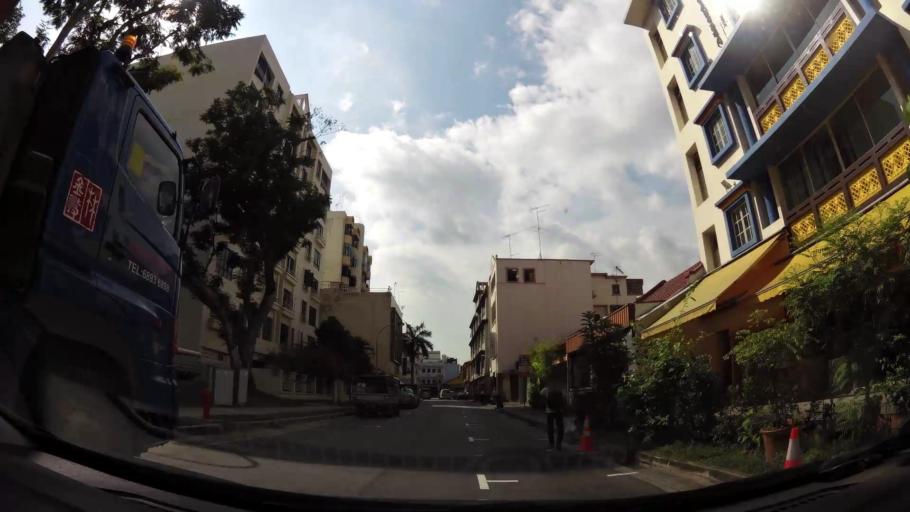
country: SG
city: Singapore
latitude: 1.3138
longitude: 103.8792
